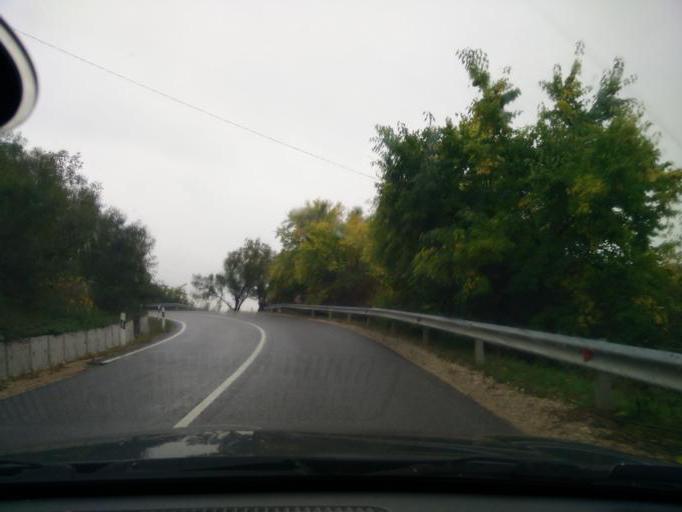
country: HU
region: Komarom-Esztergom
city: Tarjan
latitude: 47.6420
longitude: 18.5401
